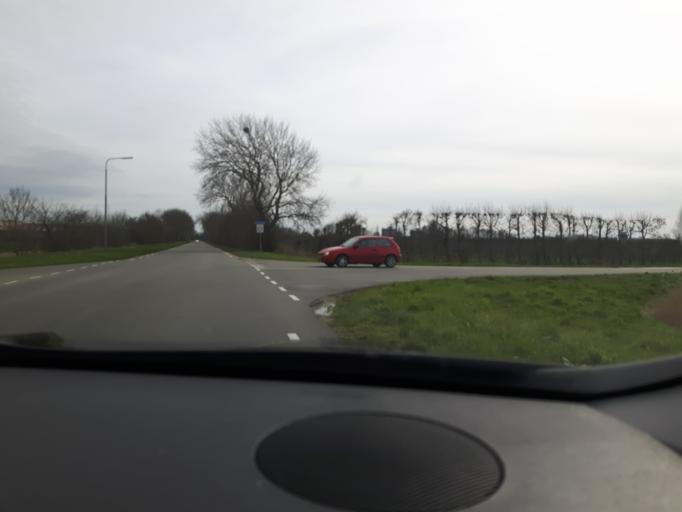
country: NL
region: Zeeland
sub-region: Gemeente Middelburg
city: Middelburg
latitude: 51.5128
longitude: 3.5995
